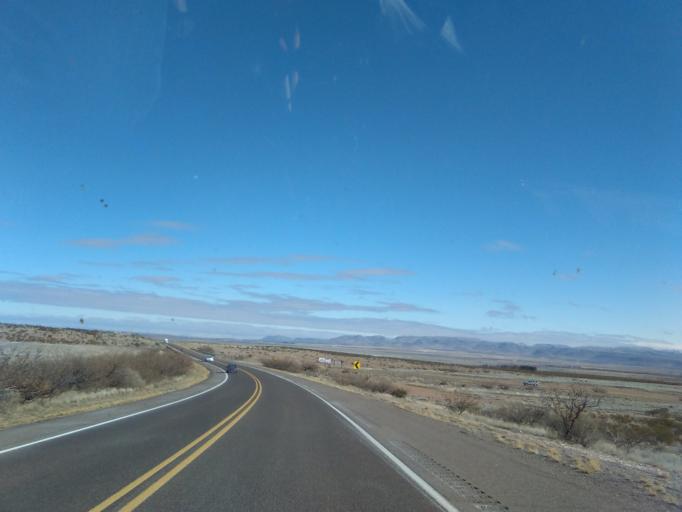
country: US
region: New Mexico
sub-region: Dona Ana County
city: Hatch
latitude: 32.5735
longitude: -107.4046
